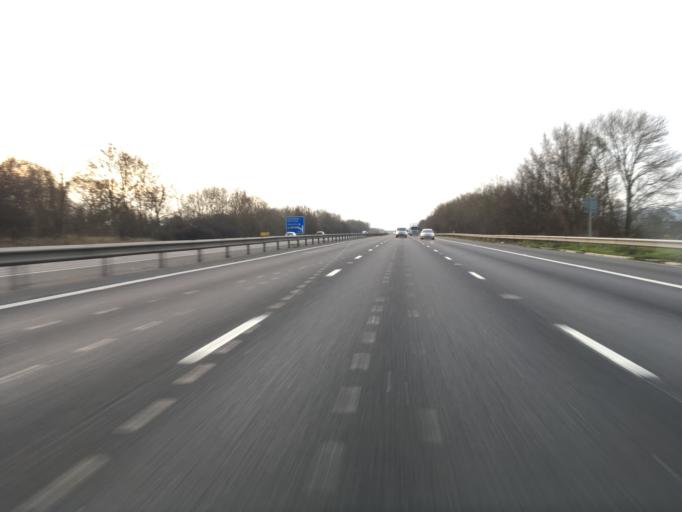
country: GB
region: England
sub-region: Gloucestershire
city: Churchdown
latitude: 51.9039
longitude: -2.1519
